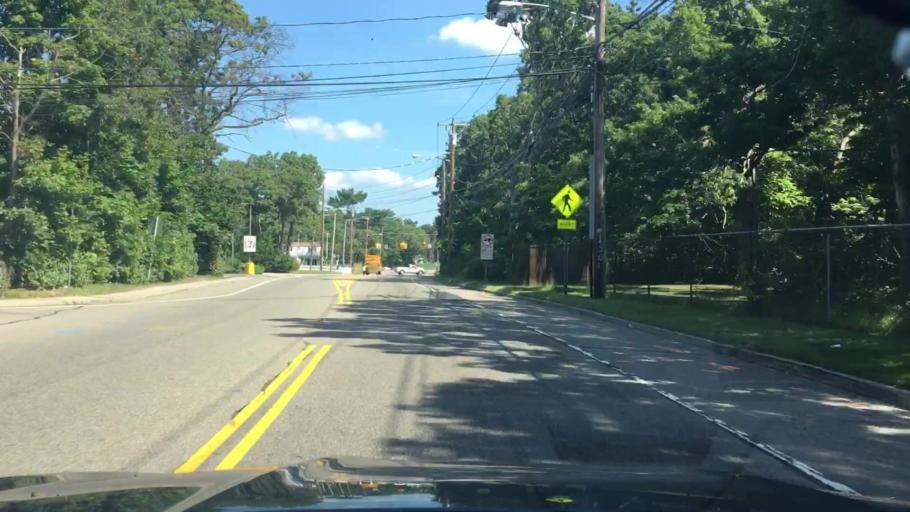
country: US
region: New York
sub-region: Suffolk County
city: Islandia
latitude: 40.8014
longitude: -73.1671
